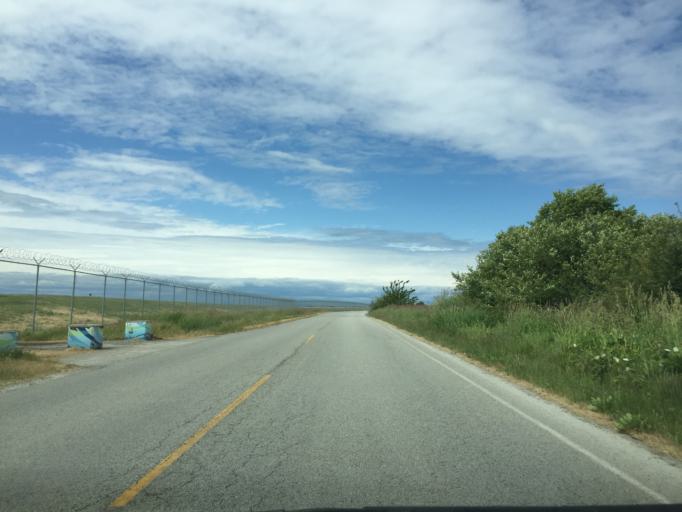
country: CA
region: British Columbia
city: Richmond
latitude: 49.2067
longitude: -123.1952
